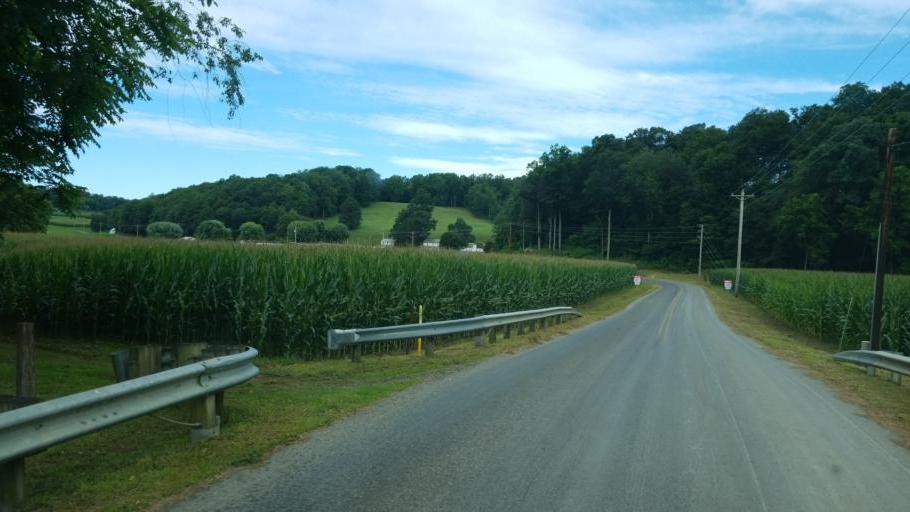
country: US
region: Ohio
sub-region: Holmes County
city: Millersburg
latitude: 40.4875
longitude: -81.8152
